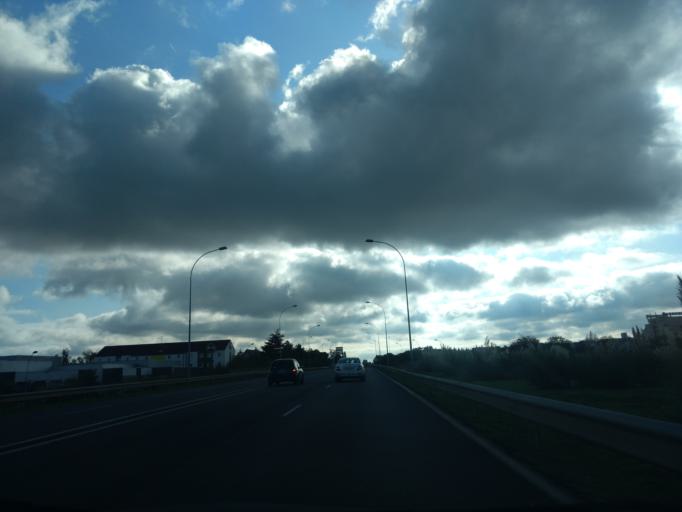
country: FR
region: Poitou-Charentes
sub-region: Departement de la Vienne
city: Chasseneuil-du-Poitou
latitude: 46.6605
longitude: 0.3691
